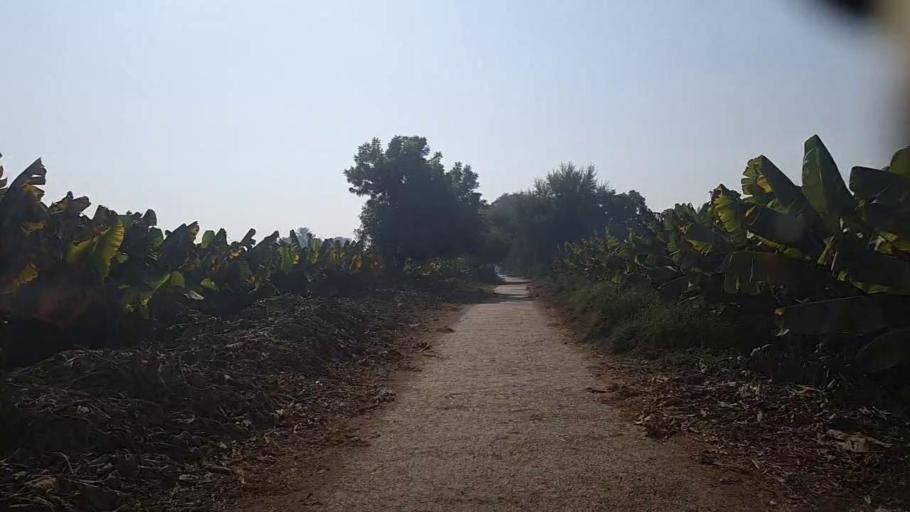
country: PK
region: Sindh
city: Kandiari
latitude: 27.0165
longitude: 68.5018
